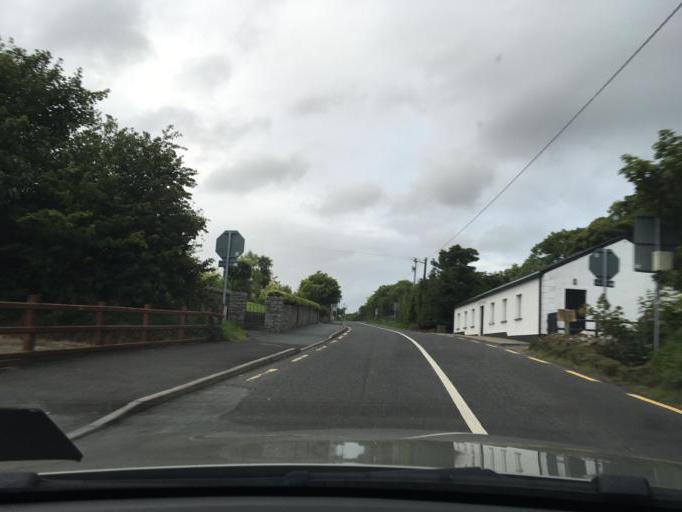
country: IE
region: Ulster
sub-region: County Donegal
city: Buncrana
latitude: 55.2625
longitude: -7.4096
